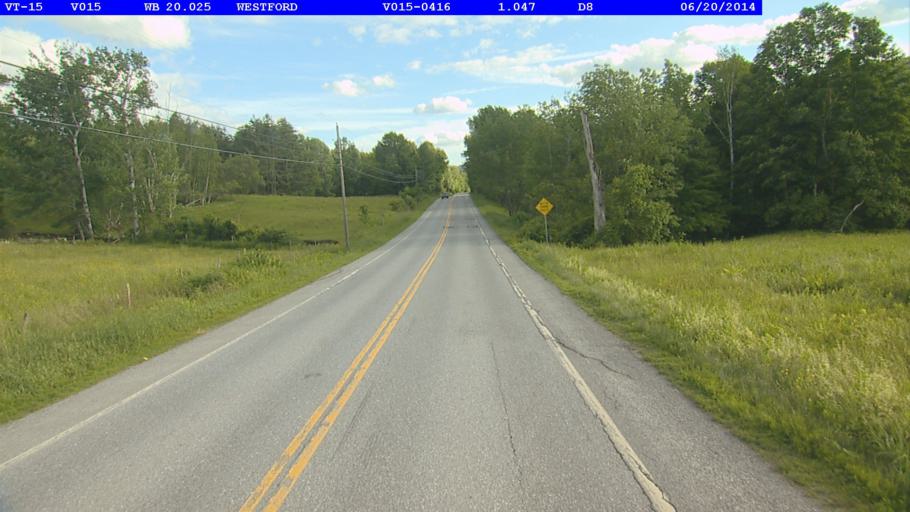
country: US
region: Vermont
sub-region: Chittenden County
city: Jericho
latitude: 44.6087
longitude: -72.9311
